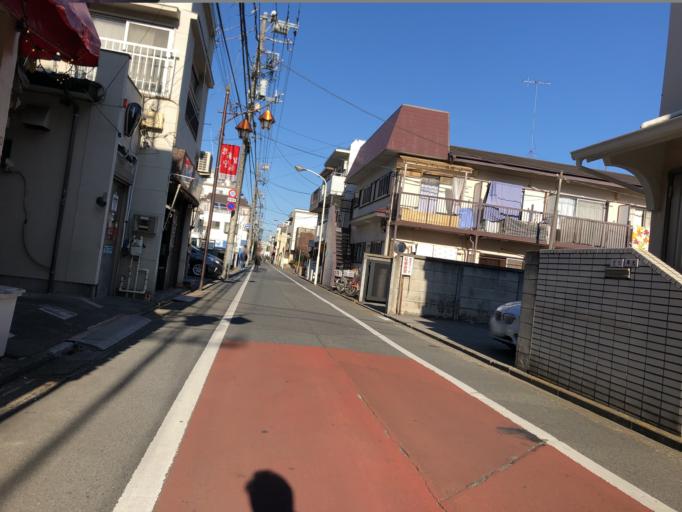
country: JP
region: Tokyo
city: Musashino
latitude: 35.7081
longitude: 139.5589
